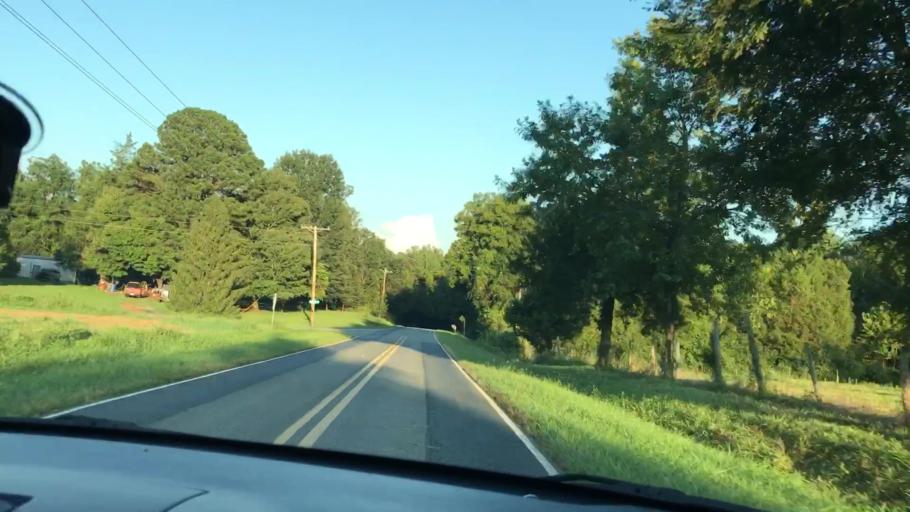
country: US
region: North Carolina
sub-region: Randolph County
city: Franklinville
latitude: 35.8002
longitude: -79.6715
